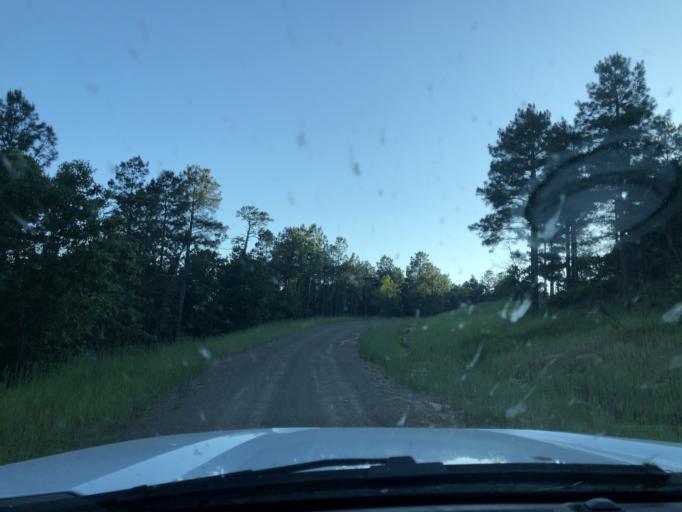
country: US
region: Oklahoma
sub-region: Le Flore County
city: Talihina
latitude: 34.5797
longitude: -95.1712
